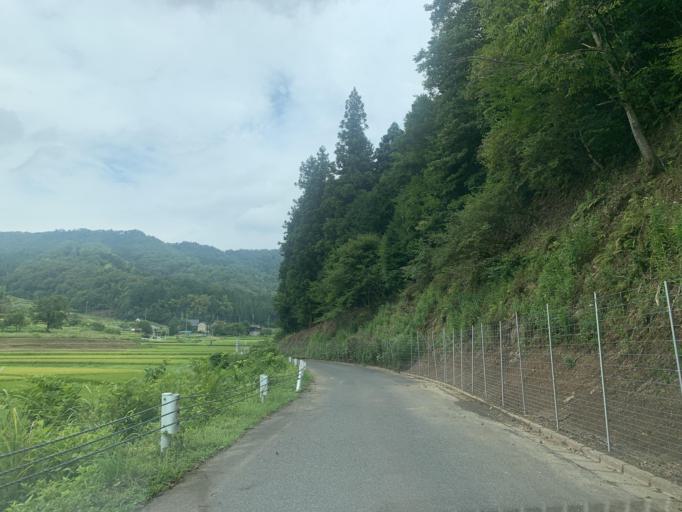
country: JP
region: Kyoto
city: Miyazu
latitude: 35.4435
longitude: 135.1602
